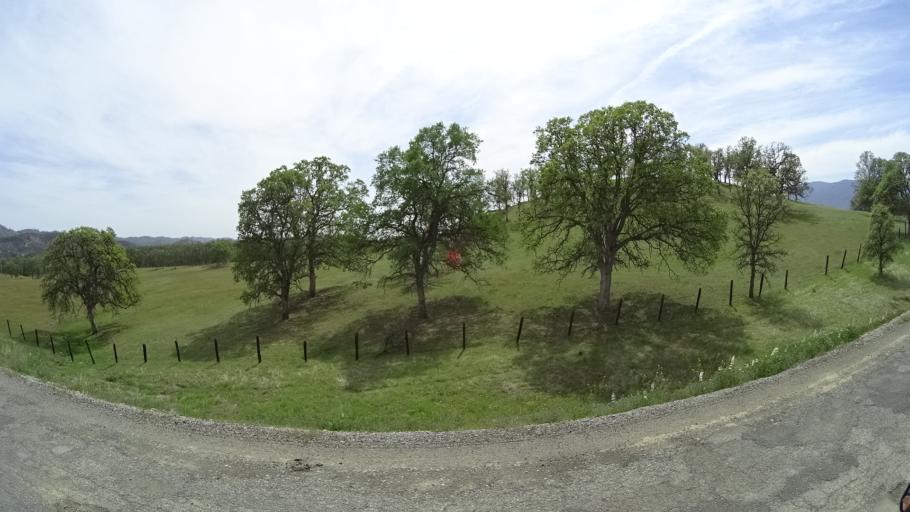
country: US
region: California
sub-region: Glenn County
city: Willows
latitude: 39.6063
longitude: -122.5537
